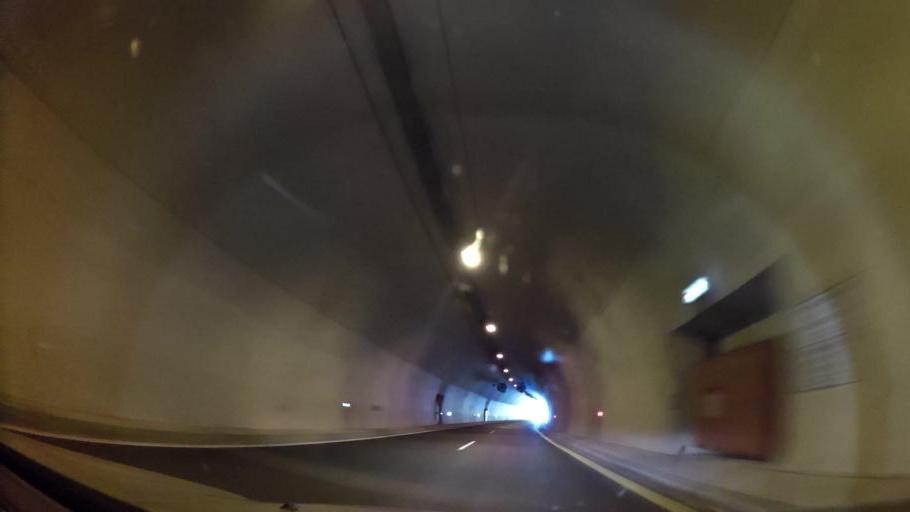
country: GR
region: Central Macedonia
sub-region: Nomos Imathias
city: Rizomata
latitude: 40.3777
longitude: 22.0911
